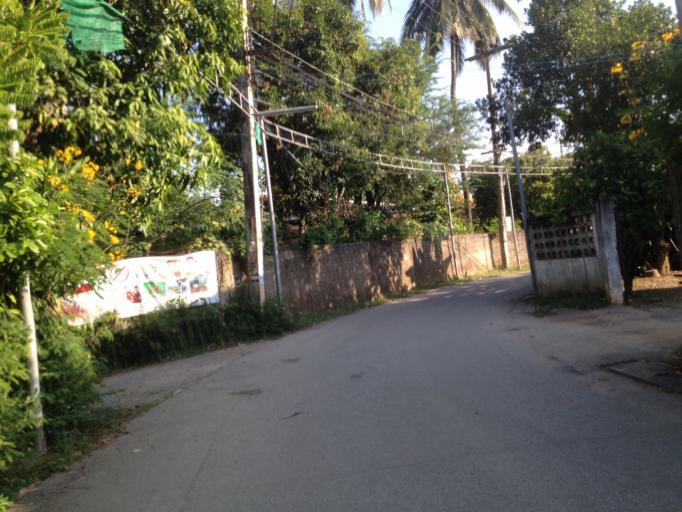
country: TH
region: Chiang Mai
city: Hang Dong
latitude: 18.7246
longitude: 98.9449
